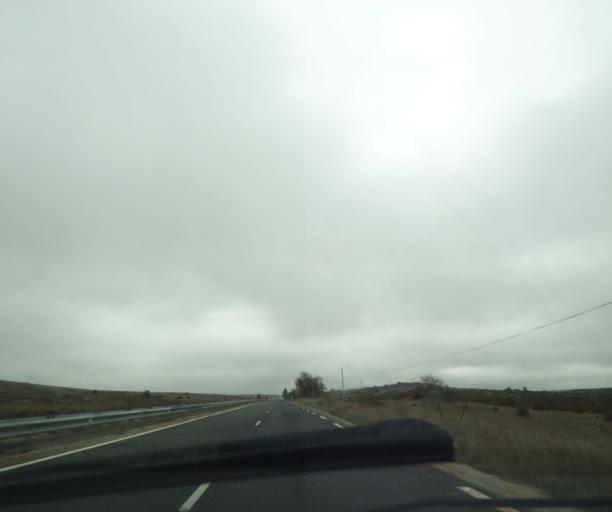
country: FR
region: Midi-Pyrenees
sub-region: Departement de l'Aveyron
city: La Cavalerie
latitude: 44.0505
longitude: 3.1324
